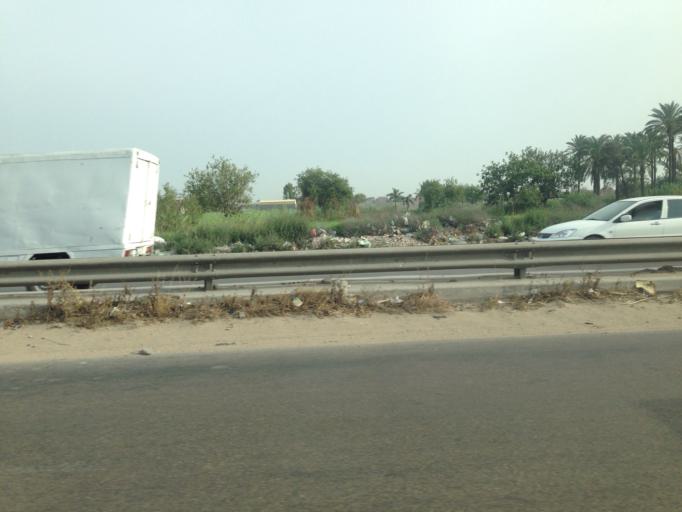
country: EG
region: Alexandria
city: Alexandria
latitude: 31.2035
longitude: 30.0122
